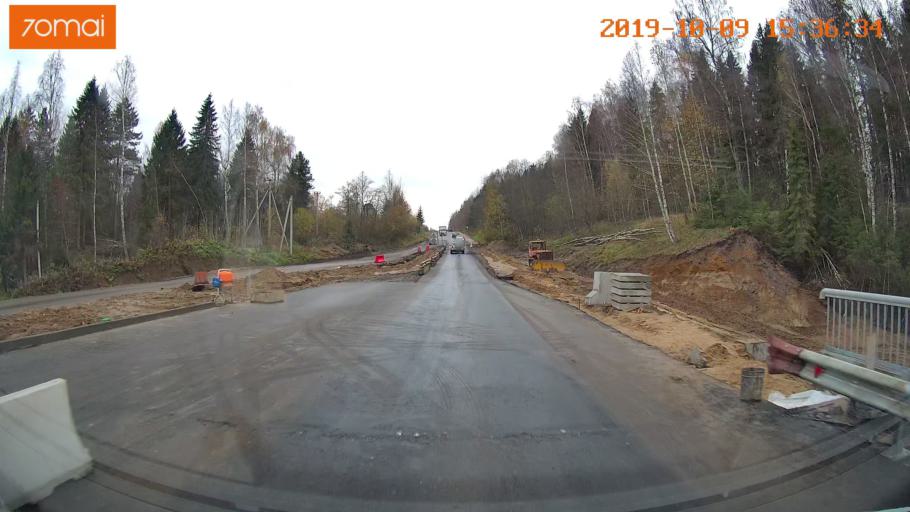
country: RU
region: Kostroma
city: Oktyabr'skiy
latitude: 57.9230
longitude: 41.2090
